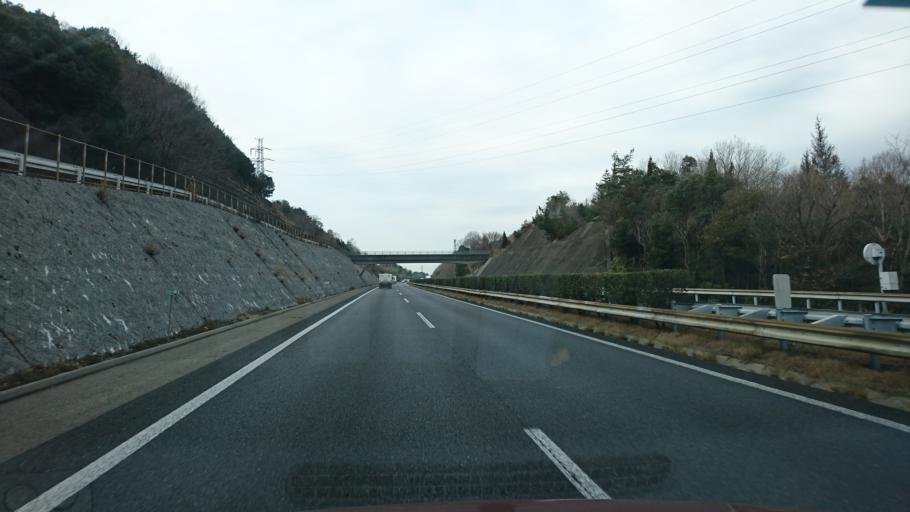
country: JP
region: Okayama
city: Kamogatacho-kamogata
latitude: 34.5344
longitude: 133.5519
